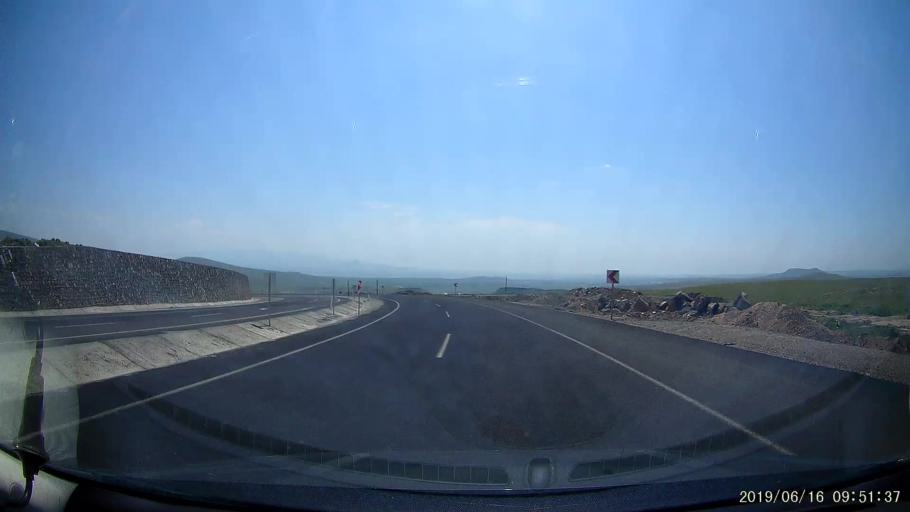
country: TR
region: Kars
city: Digor
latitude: 40.3905
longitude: 43.3698
